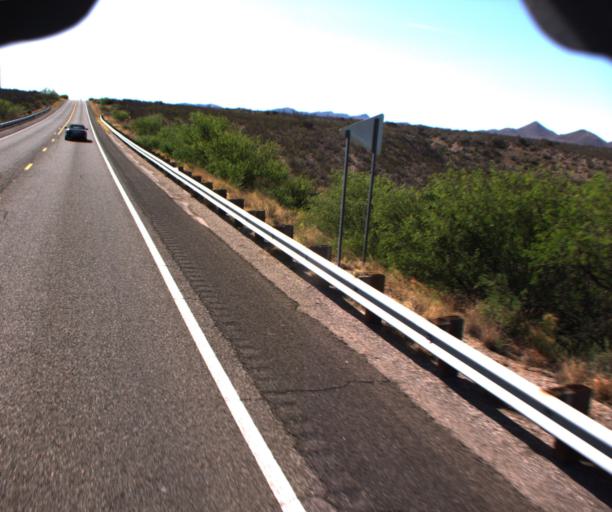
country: US
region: Arizona
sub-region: Cochise County
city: Tombstone
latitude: 31.7718
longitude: -110.1261
